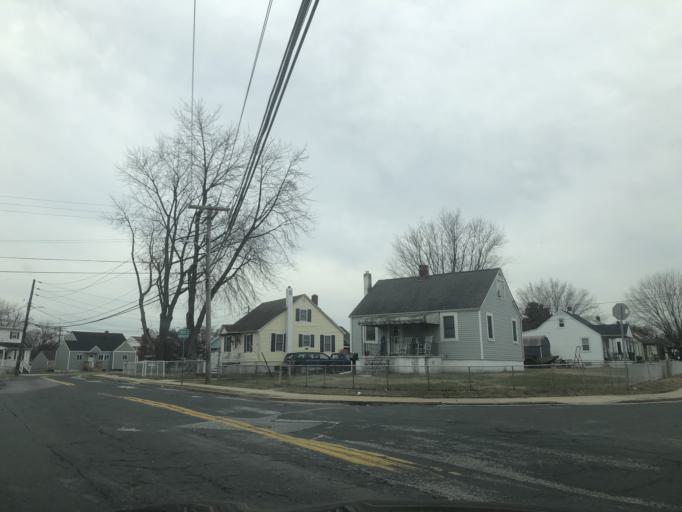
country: US
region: Maryland
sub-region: Baltimore County
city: Dundalk
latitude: 39.2632
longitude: -76.4873
